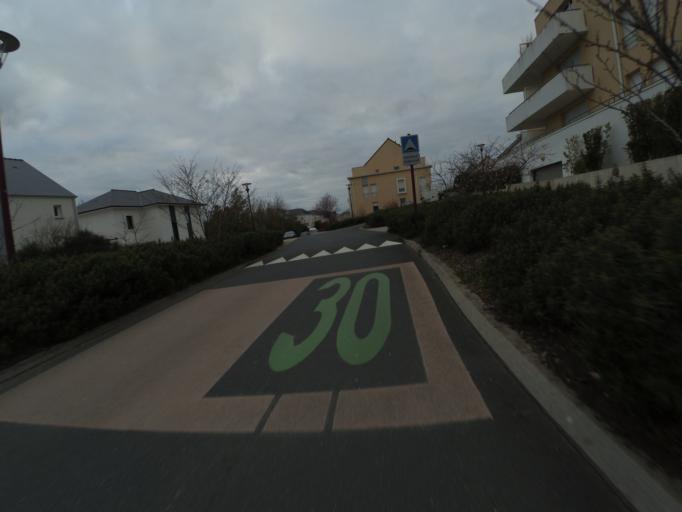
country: FR
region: Pays de la Loire
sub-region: Departement de la Loire-Atlantique
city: Carquefou
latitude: 47.3065
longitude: -1.4831
